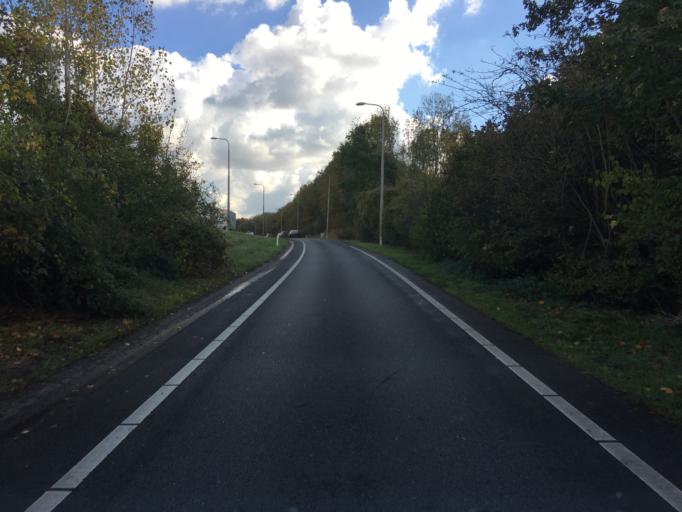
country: NL
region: Gelderland
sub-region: Gemeente Arnhem
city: Arnhem
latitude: 51.9587
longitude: 5.9044
